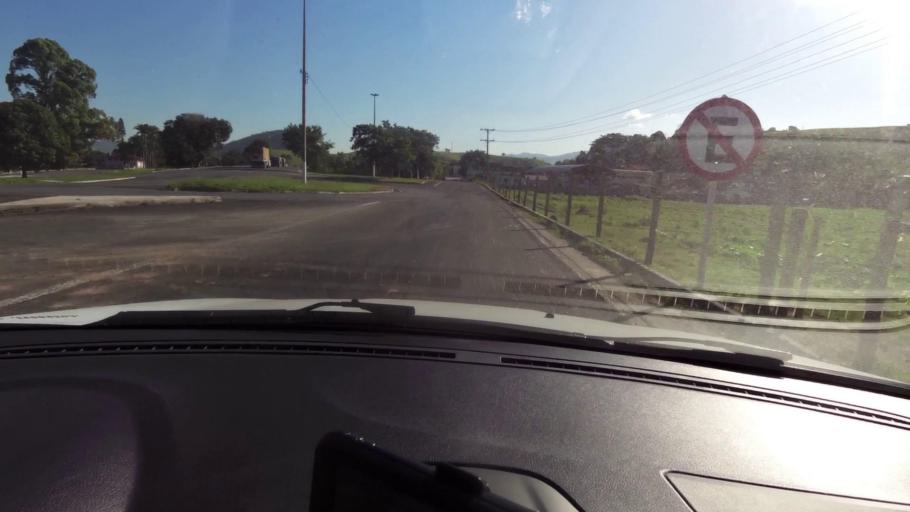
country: BR
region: Espirito Santo
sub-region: Alfredo Chaves
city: Alfredo Chaves
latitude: -20.6858
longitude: -40.6747
